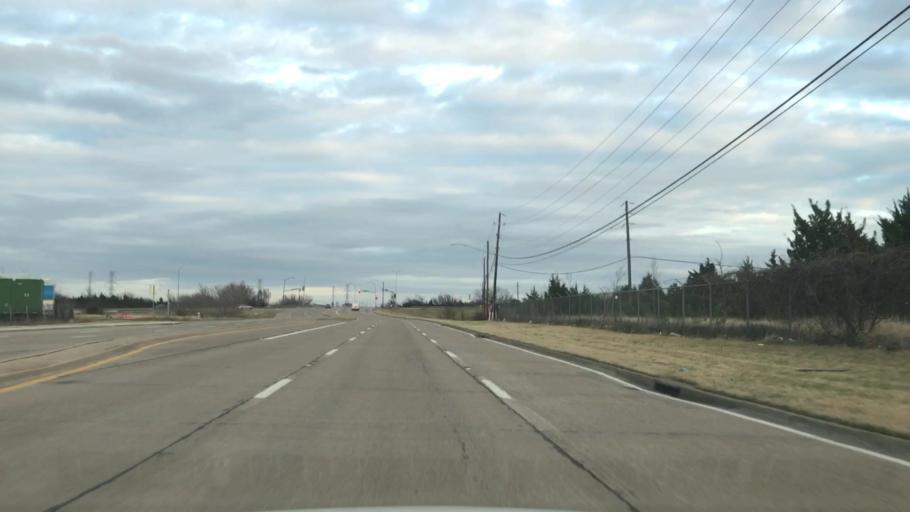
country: US
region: Texas
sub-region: Dallas County
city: Cockrell Hill
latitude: 32.7056
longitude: -96.9068
